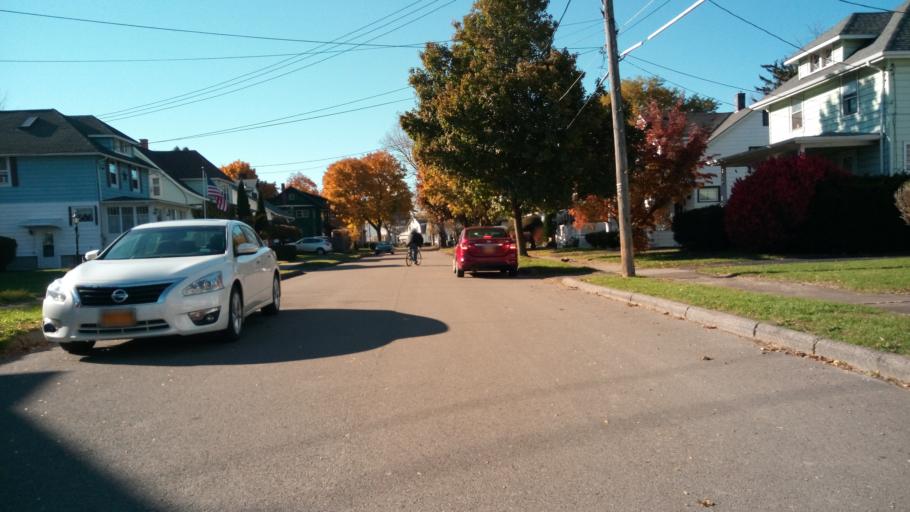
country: US
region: New York
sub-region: Chemung County
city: Southport
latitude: 42.0686
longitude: -76.8050
